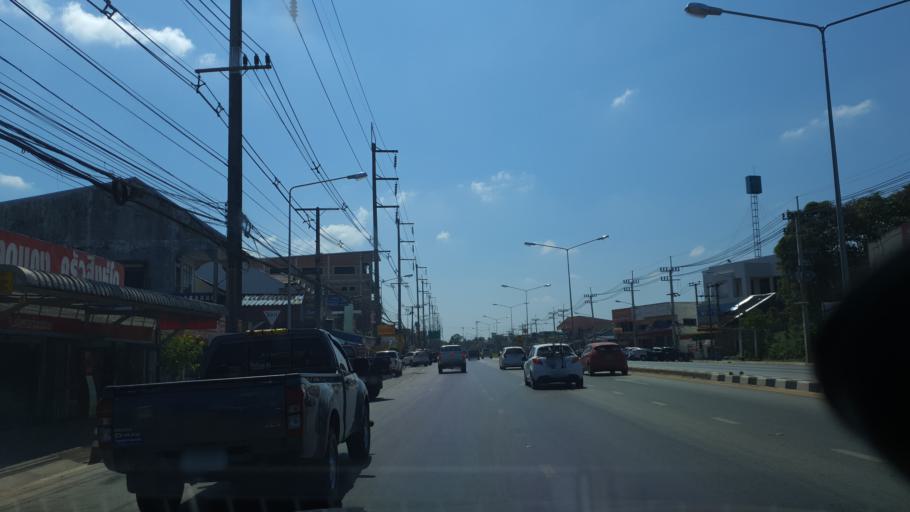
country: TH
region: Krabi
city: Khlong Thom
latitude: 7.9416
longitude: 99.1445
